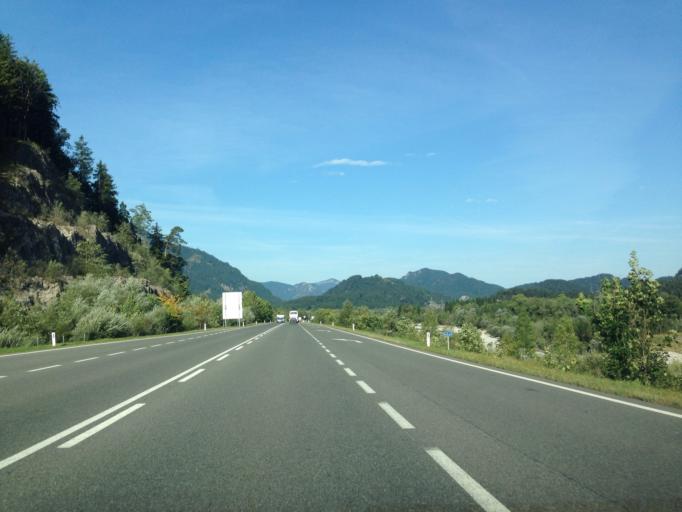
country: AT
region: Tyrol
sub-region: Politischer Bezirk Reutte
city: Pflach
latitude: 47.5257
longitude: 10.6996
